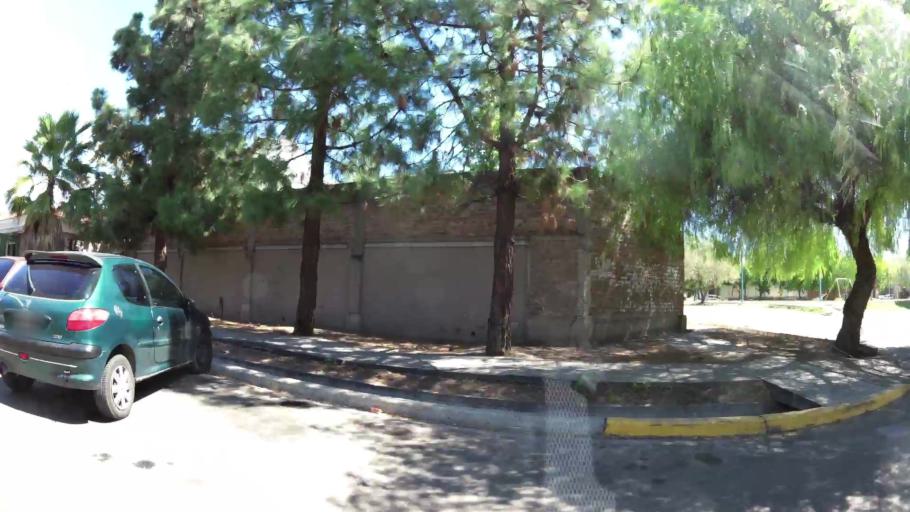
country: AR
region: Mendoza
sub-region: Departamento de Godoy Cruz
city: Godoy Cruz
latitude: -32.9510
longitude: -68.8624
